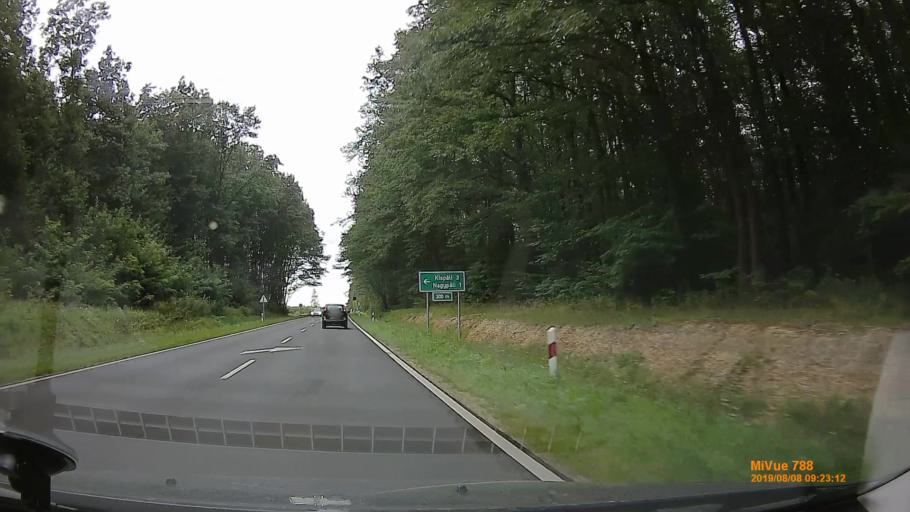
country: HU
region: Zala
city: Zalaegerszeg
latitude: 46.9057
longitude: 16.8584
